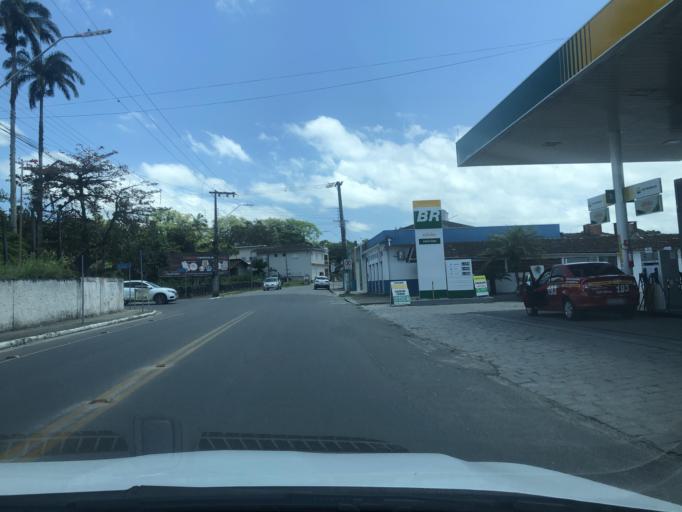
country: BR
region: Santa Catarina
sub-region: Sao Francisco Do Sul
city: Sao Francisco do Sul
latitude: -26.2508
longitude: -48.6416
